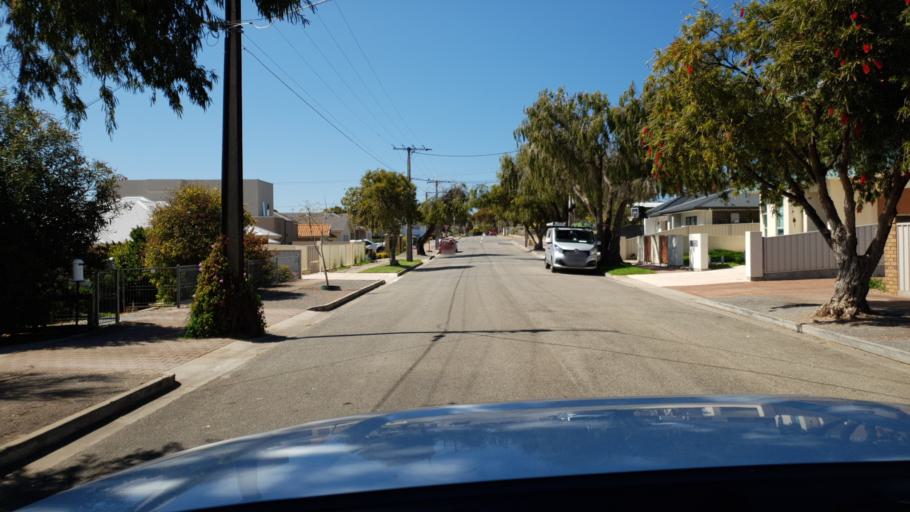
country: AU
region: South Australia
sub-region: Holdfast Bay
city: Seacliff Park
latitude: -35.0276
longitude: 138.5314
